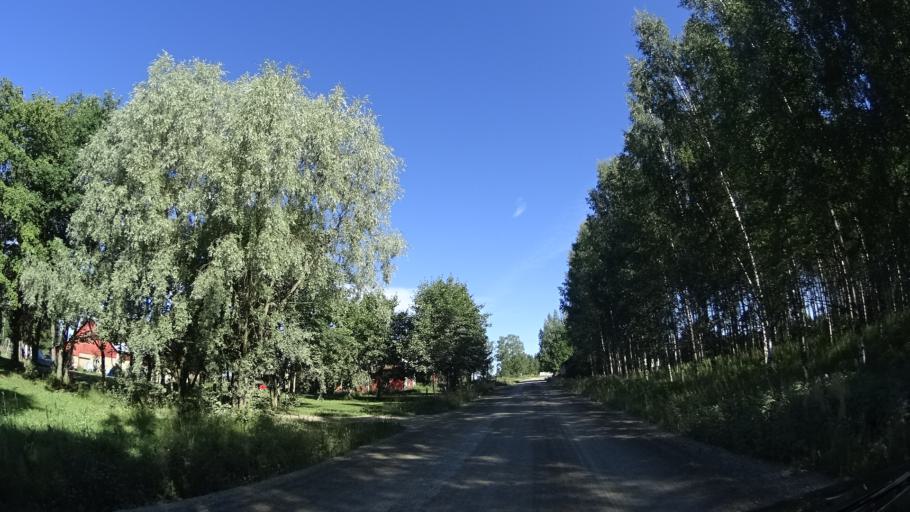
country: FI
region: Central Finland
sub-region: Jyvaeskylae
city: Petaejaevesi
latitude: 62.3612
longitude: 25.3184
